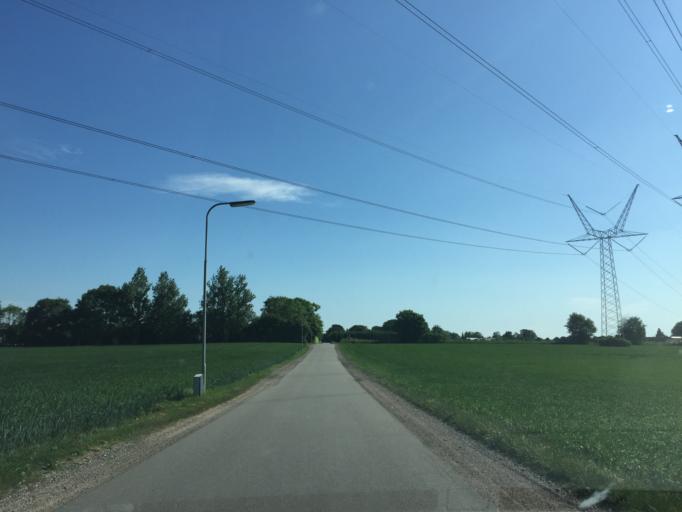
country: DK
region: South Denmark
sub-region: Odense Kommune
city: Hojby
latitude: 55.3374
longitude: 10.3960
